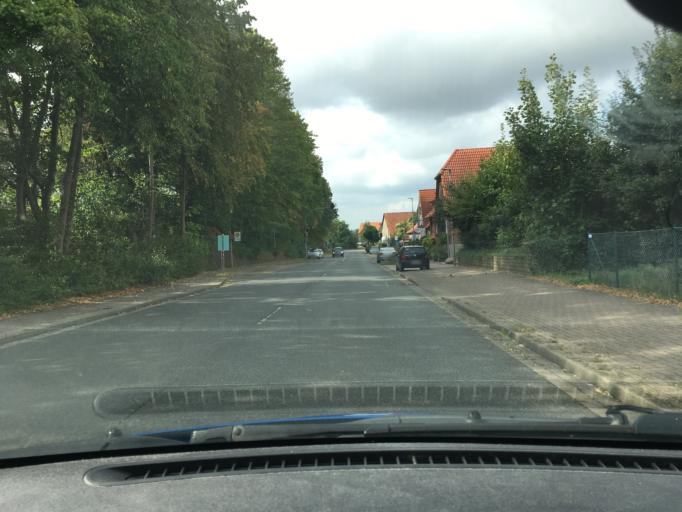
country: DE
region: Lower Saxony
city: Messenkamp
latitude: 52.2331
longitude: 9.4171
